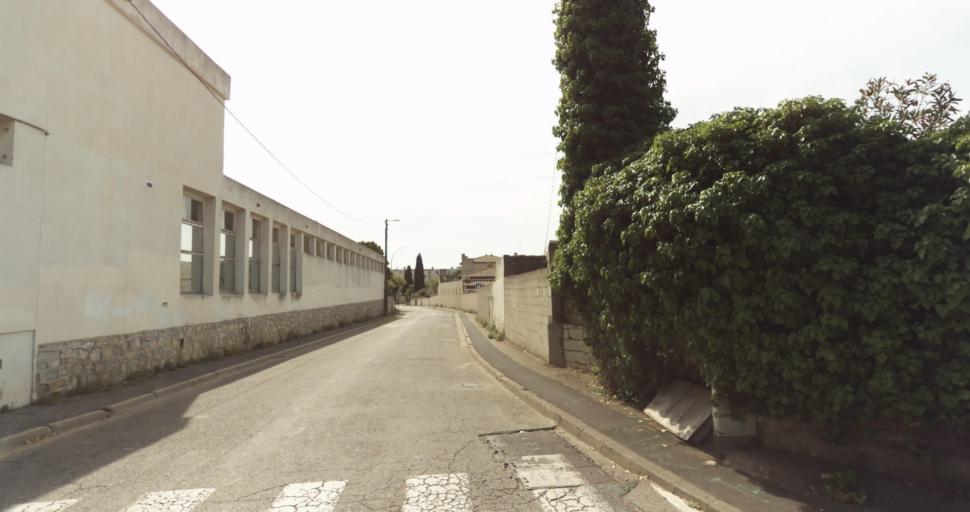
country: FR
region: Languedoc-Roussillon
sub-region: Departement du Gard
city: Rodilhan
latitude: 43.8571
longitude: 4.3959
